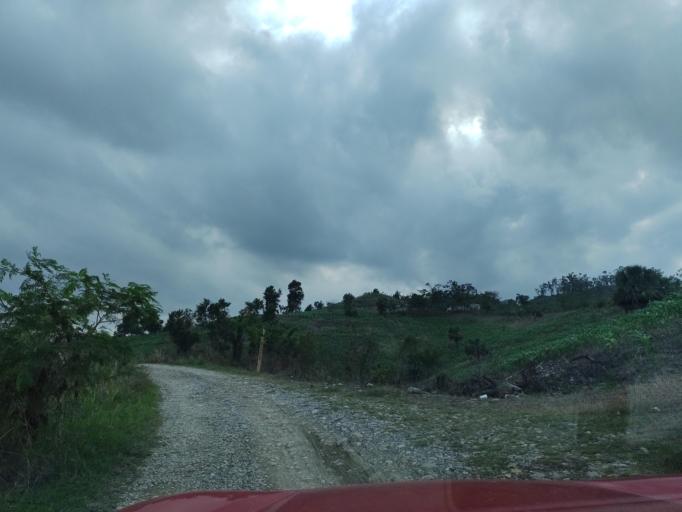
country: MX
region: Veracruz
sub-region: Papantla
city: El Chote
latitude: 20.4399
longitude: -97.4056
